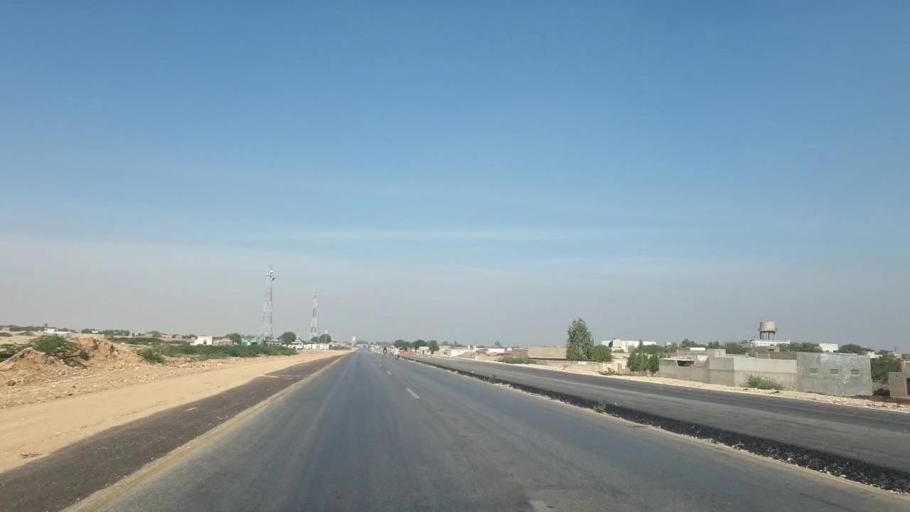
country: PK
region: Sindh
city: Hala
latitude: 25.6987
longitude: 68.2956
